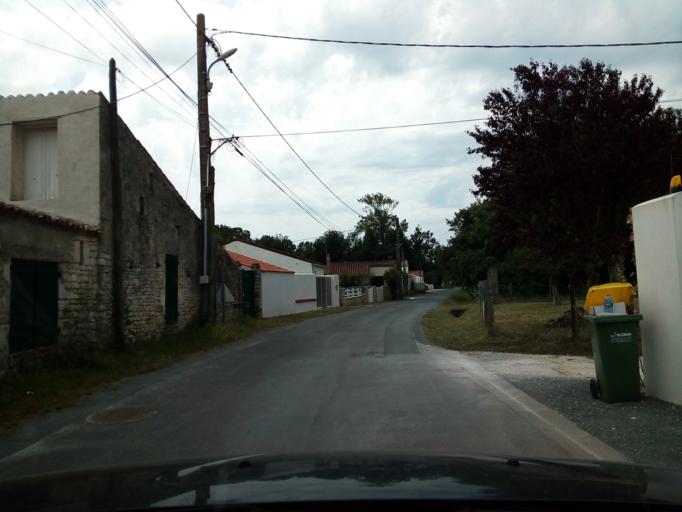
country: FR
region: Poitou-Charentes
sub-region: Departement de la Charente-Maritime
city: Dolus-d'Oleron
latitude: 45.9238
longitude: -1.2723
